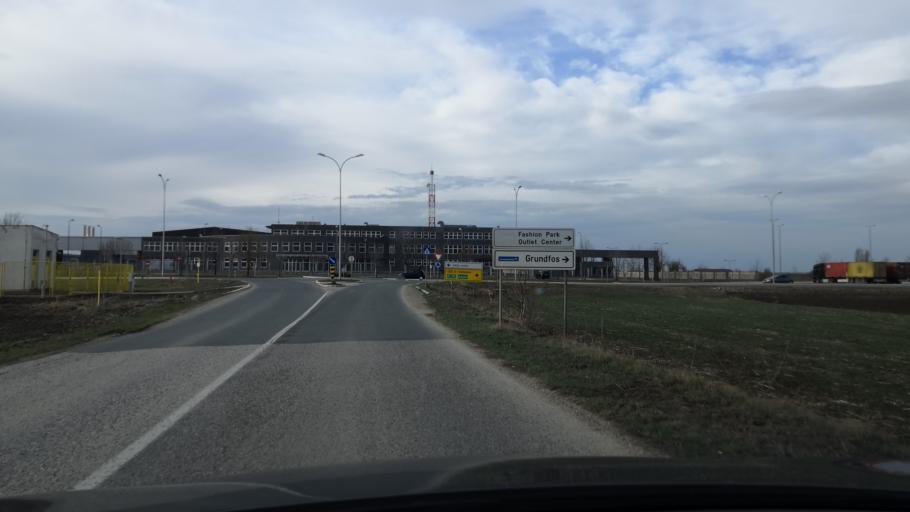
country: RS
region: Autonomna Pokrajina Vojvodina
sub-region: Sremski Okrug
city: Ingija
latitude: 45.0548
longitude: 20.1037
